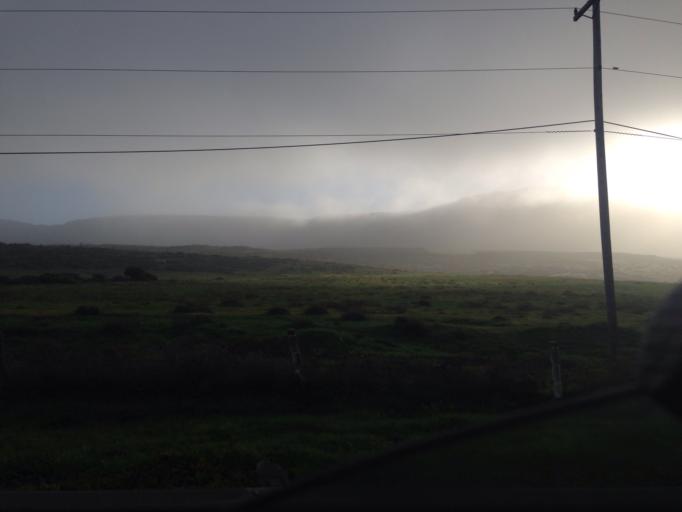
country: MX
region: Baja California
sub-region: Playas de Rosarito
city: Santa Anita
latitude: 32.0795
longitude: -116.8802
